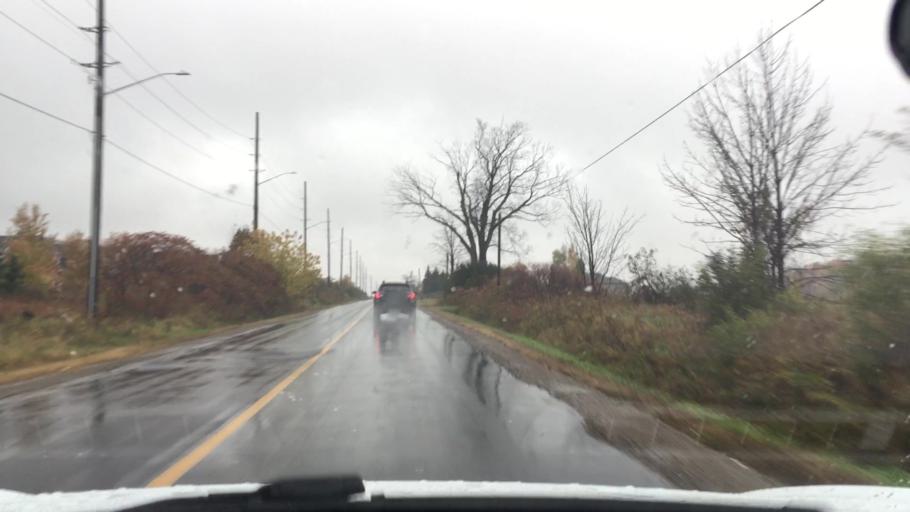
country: CA
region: Ontario
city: Oshawa
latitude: 43.9502
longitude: -78.8325
